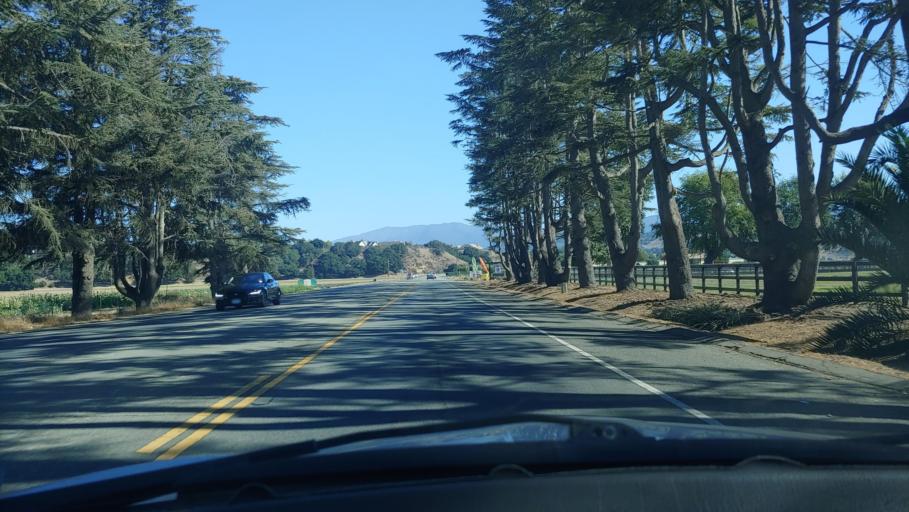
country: US
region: California
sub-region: Santa Barbara County
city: Solvang
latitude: 34.5996
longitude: -120.1613
